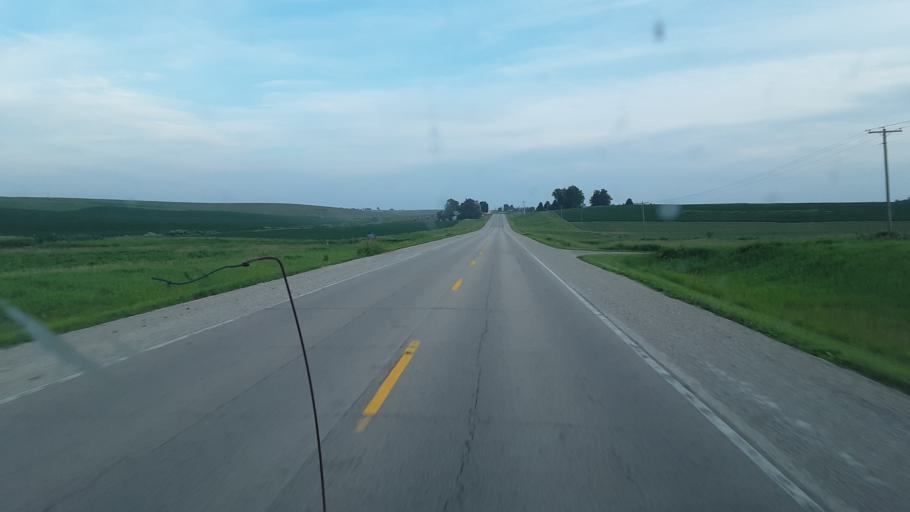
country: US
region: Iowa
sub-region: Benton County
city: Belle Plaine
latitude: 41.7847
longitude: -92.2793
